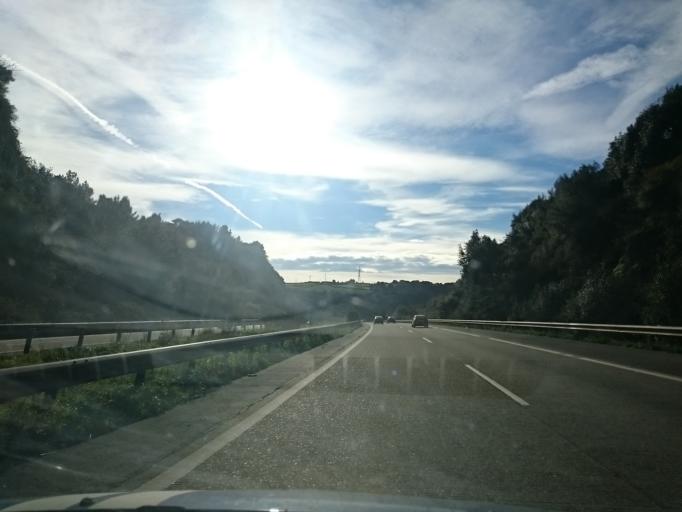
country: ES
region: Asturias
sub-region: Province of Asturias
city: Natahoyo
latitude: 43.5096
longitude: -5.7393
